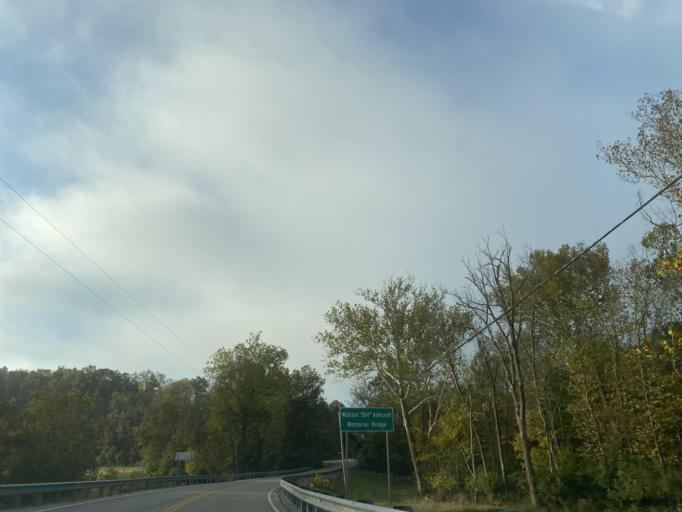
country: US
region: Kentucky
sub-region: Pendleton County
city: Falmouth
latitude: 38.7212
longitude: -84.3000
